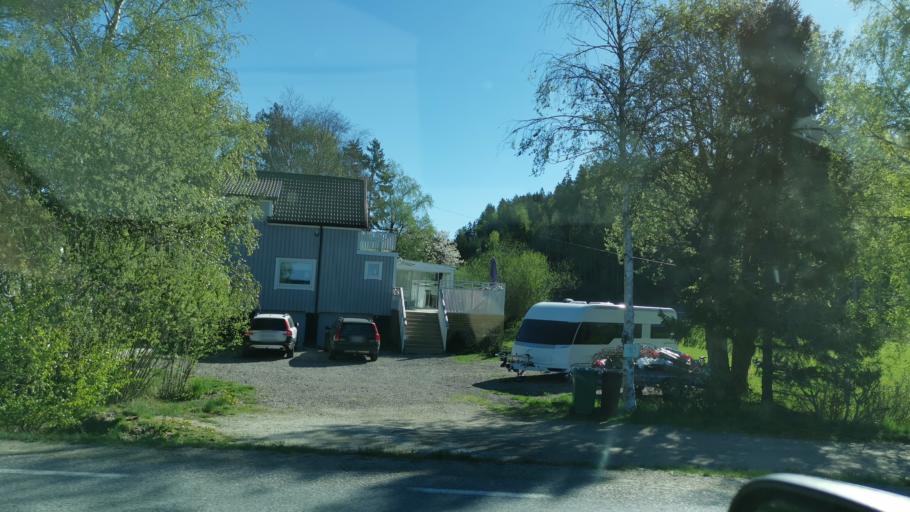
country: SE
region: Vaestra Goetaland
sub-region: Uddevalla Kommun
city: Uddevalla
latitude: 58.2959
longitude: 11.8977
